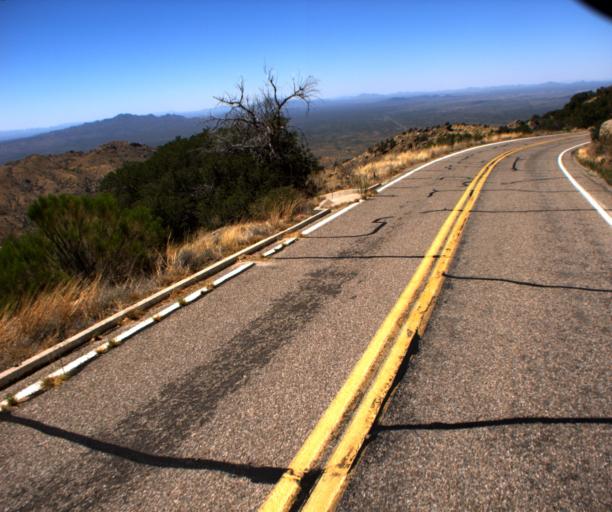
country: US
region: Arizona
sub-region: Pima County
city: Sells
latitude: 31.9662
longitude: -111.6206
